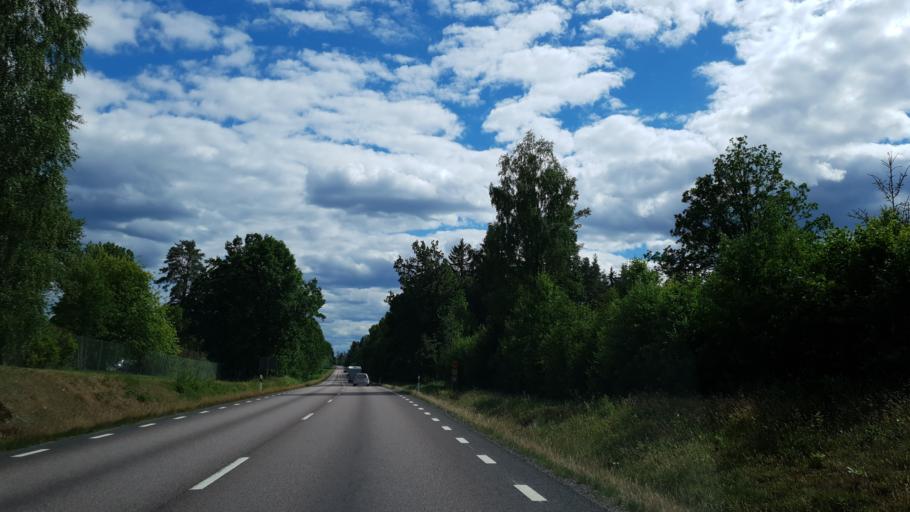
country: SE
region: Kronoberg
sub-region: Lessebo Kommun
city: Lessebo
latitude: 56.8448
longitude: 15.3894
